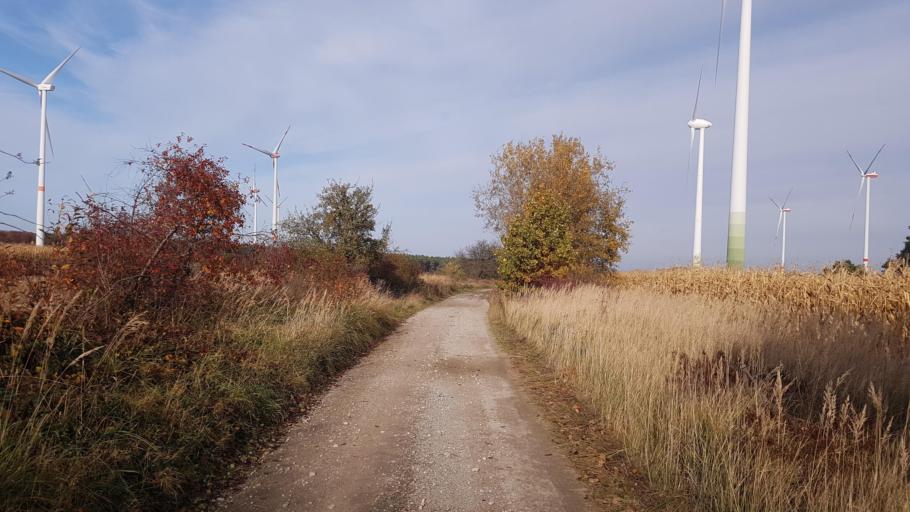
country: DE
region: Brandenburg
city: Treuenbrietzen
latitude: 52.0090
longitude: 12.8802
